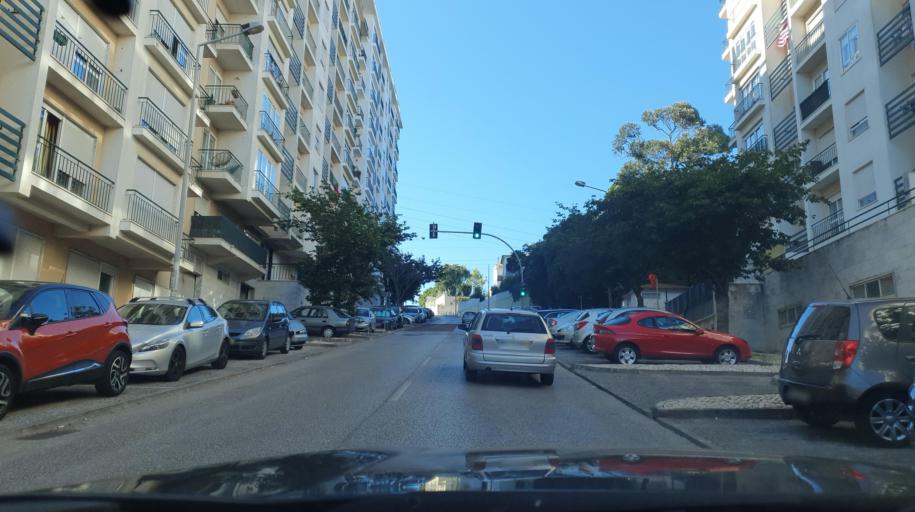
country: PT
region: Lisbon
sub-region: Sintra
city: Cacem
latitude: 38.7592
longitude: -9.2822
